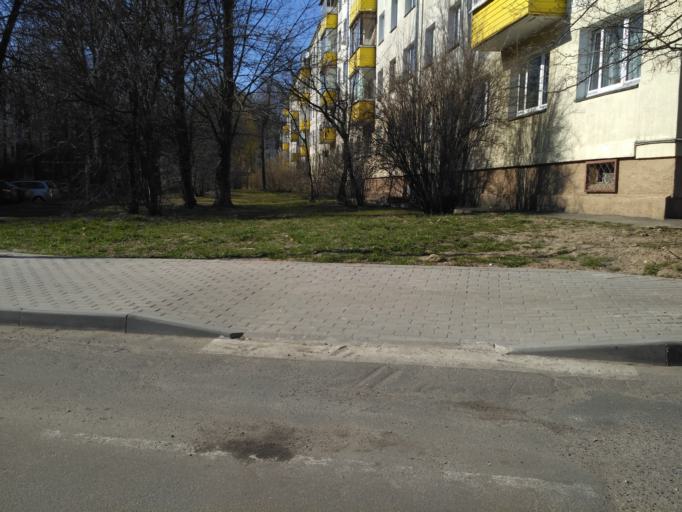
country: BY
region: Minsk
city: Minsk
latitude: 53.9031
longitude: 27.5092
